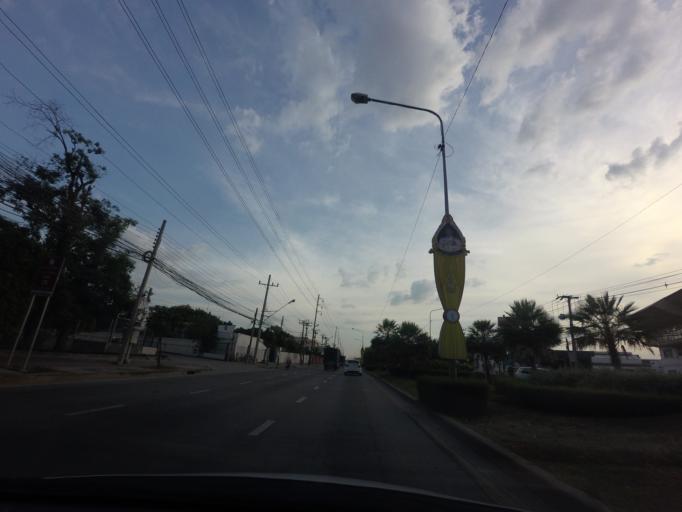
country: TH
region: Bangkok
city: Bang Khun Thian
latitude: 13.6373
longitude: 100.4329
